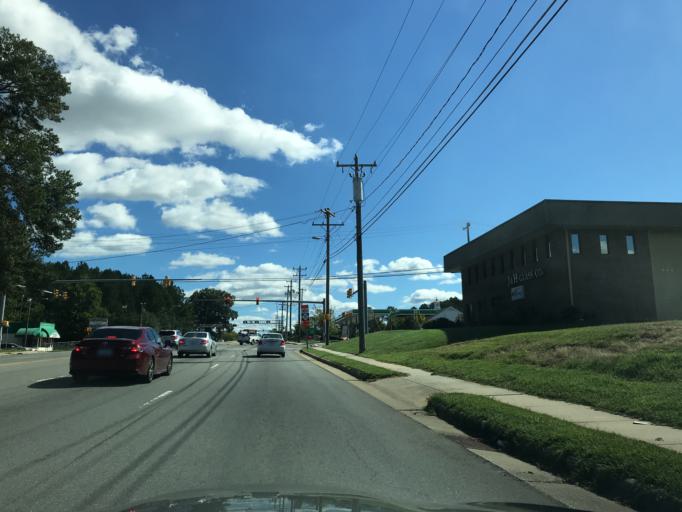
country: US
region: North Carolina
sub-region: Durham County
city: Durham
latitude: 35.9906
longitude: -78.8604
